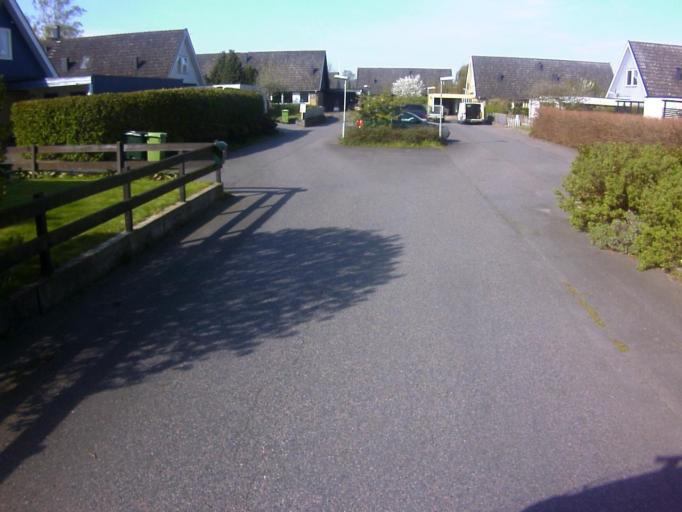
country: SE
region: Skane
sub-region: Kavlinge Kommun
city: Loddekopinge
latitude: 55.7606
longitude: 13.0040
